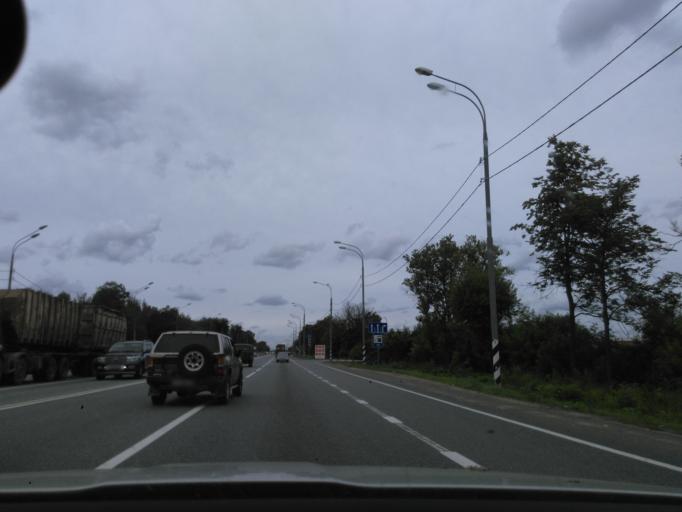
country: RU
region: Moskovskaya
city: Klin
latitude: 56.3084
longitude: 36.7822
